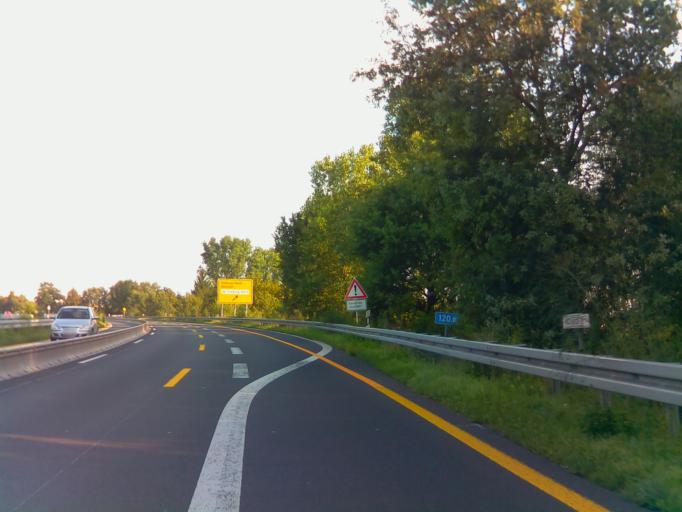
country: DE
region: Hesse
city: Dieburg
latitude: 49.9158
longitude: 8.8472
